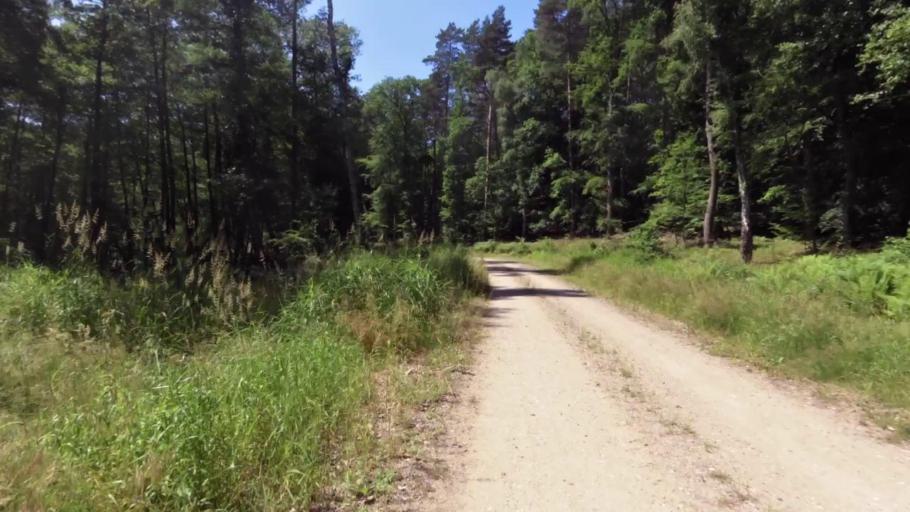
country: PL
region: West Pomeranian Voivodeship
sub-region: Powiat swidwinski
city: Polczyn-Zdroj
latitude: 53.8028
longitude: 16.1175
